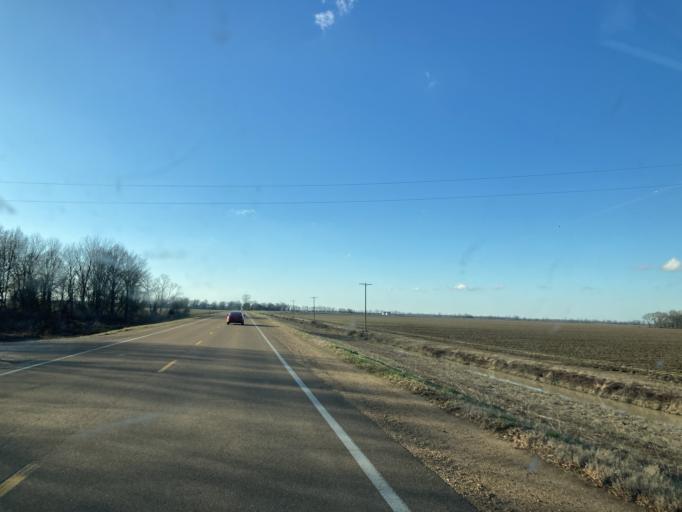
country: US
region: Mississippi
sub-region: Yazoo County
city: Yazoo City
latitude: 32.9249
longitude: -90.5737
